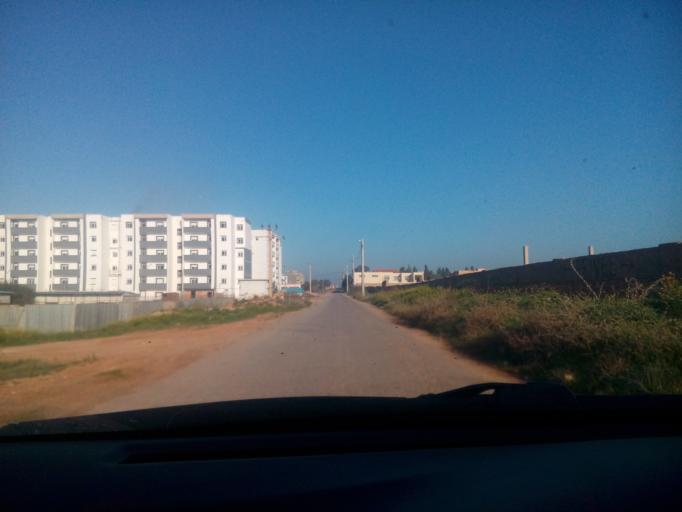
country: DZ
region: Oran
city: Bir el Djir
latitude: 35.7532
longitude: -0.5295
